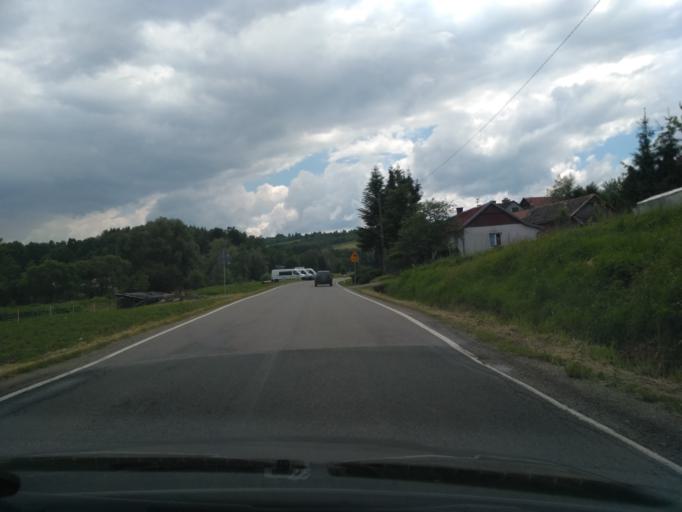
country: PL
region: Subcarpathian Voivodeship
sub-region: Powiat przeworski
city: Jawornik Polski
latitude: 49.9055
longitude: 22.3079
